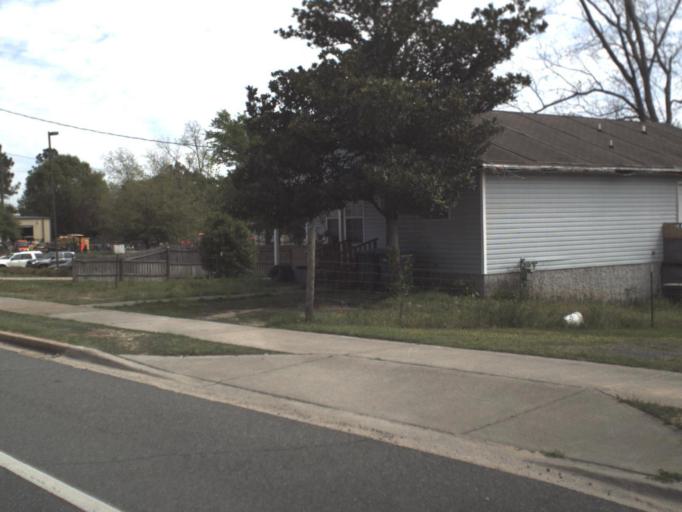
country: US
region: Florida
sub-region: Okaloosa County
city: Crestview
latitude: 30.7467
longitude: -86.5638
